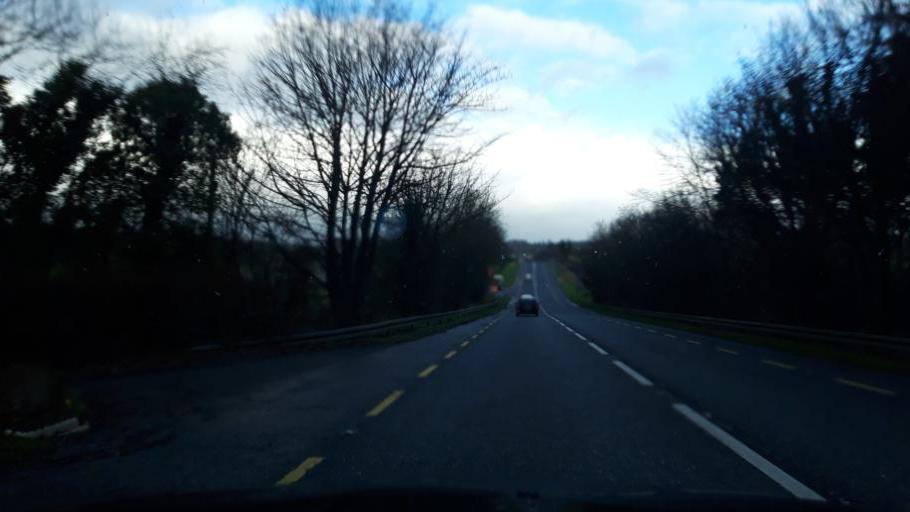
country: IE
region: Leinster
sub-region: Lu
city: Tullyallen
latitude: 53.7678
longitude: -6.4923
